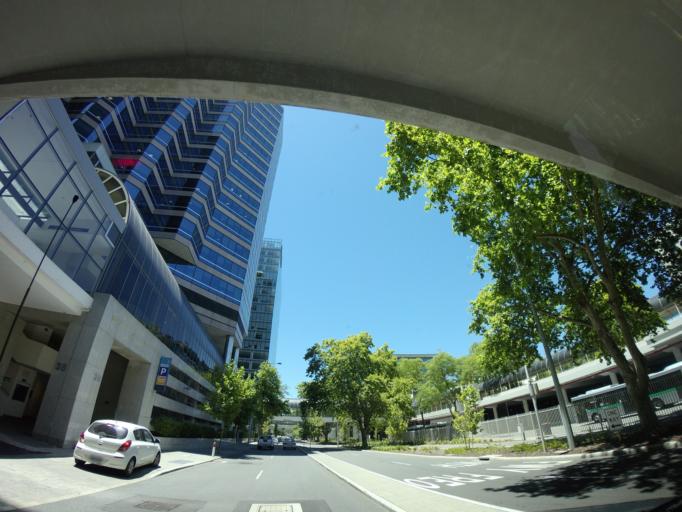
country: AU
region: Western Australia
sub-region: Cambridge
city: Perth
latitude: -31.9554
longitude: 115.8535
